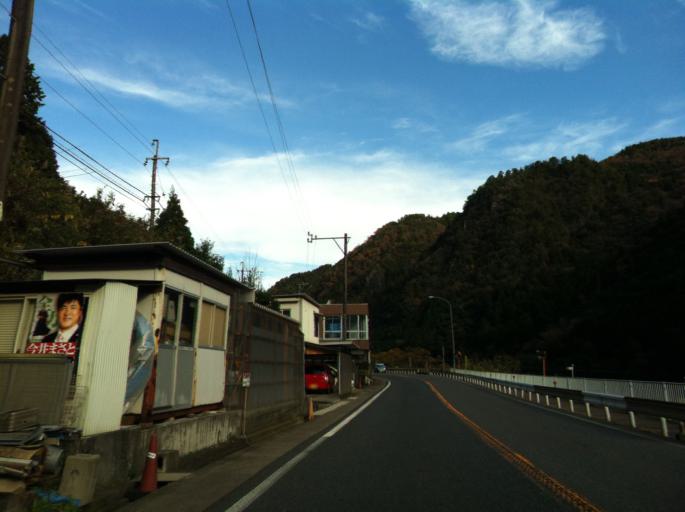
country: JP
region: Gifu
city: Mitake
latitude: 35.5866
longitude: 137.1721
